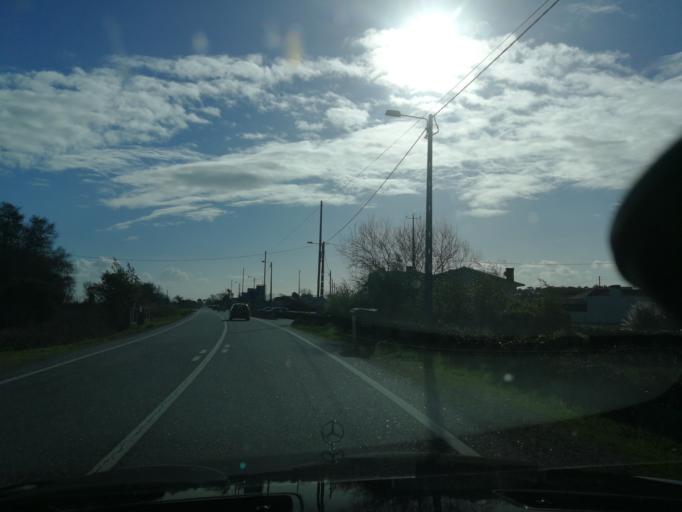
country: PT
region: Aveiro
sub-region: Estarreja
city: Pardilho
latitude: 40.8197
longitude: -8.6695
